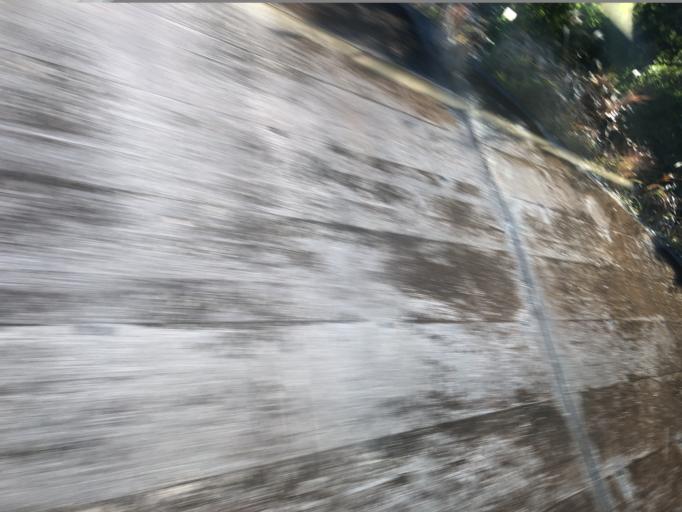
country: JP
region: Kochi
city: Nakamura
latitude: 33.0108
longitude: 132.9895
